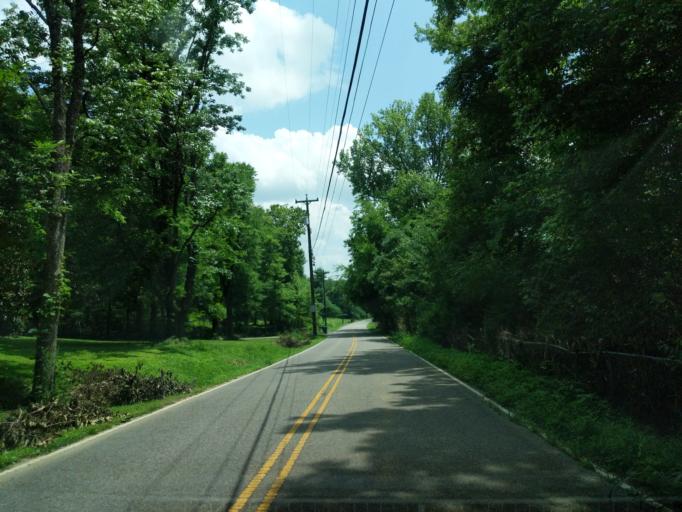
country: US
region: Tennessee
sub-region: Davidson County
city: Goodlettsville
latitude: 36.3120
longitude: -86.7332
